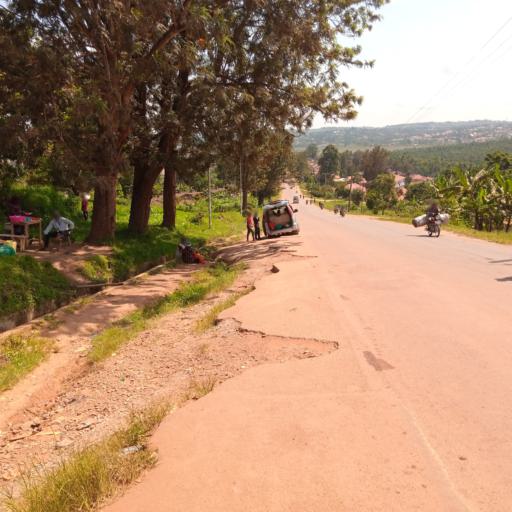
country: UG
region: Central Region
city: Masaka
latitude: -0.3431
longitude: 31.7339
